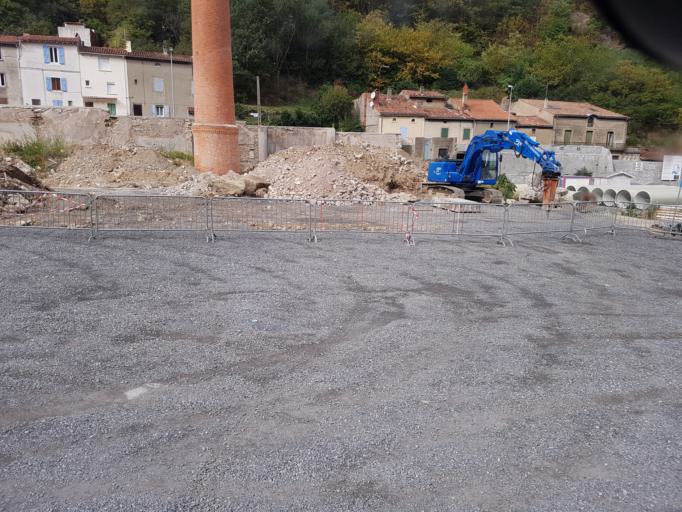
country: FR
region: Midi-Pyrenees
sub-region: Departement du Tarn
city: Mazamet
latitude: 43.4810
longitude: 2.3769
